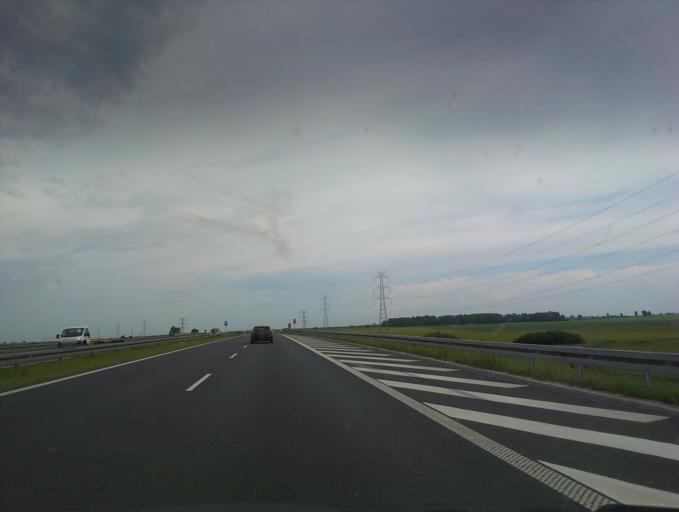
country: PL
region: Opole Voivodeship
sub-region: Powiat brzeski
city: Olszanka
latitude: 50.7496
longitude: 17.4437
